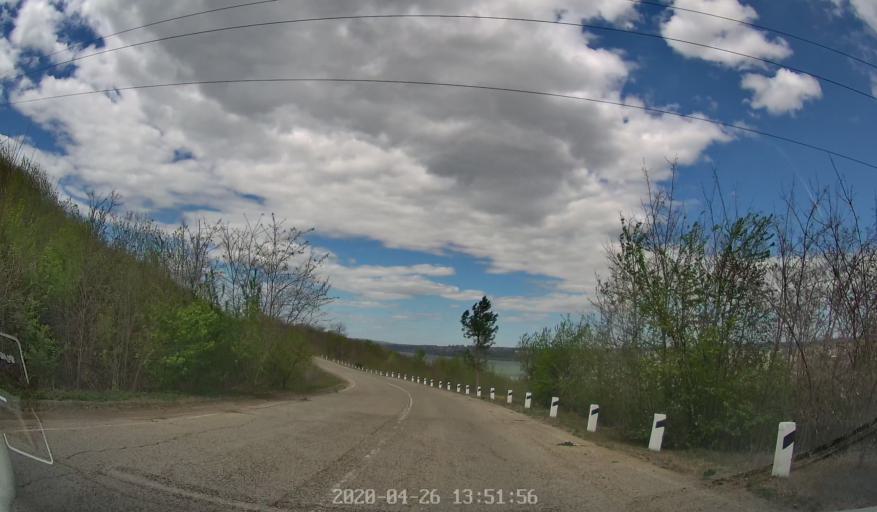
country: MD
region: Telenesti
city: Cocieri
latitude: 47.2703
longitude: 29.1210
